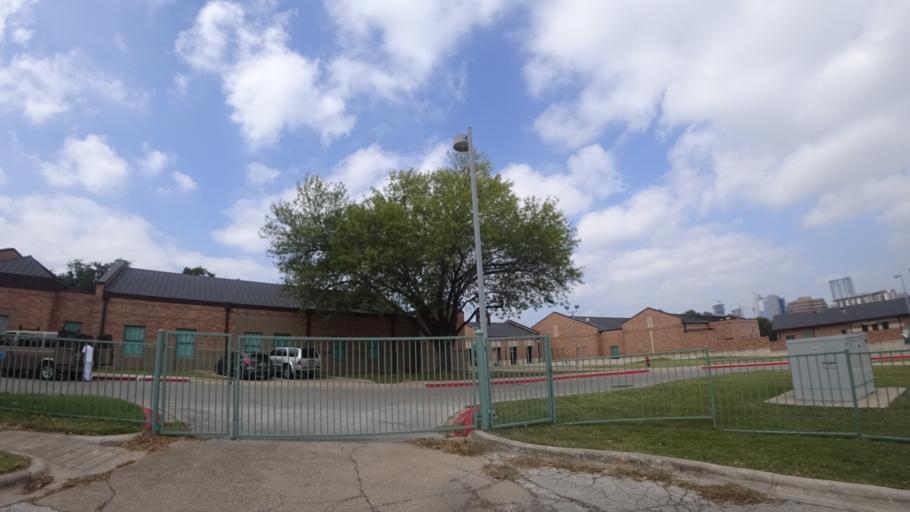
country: US
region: Texas
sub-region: Travis County
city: Austin
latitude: 30.2526
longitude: -97.7499
